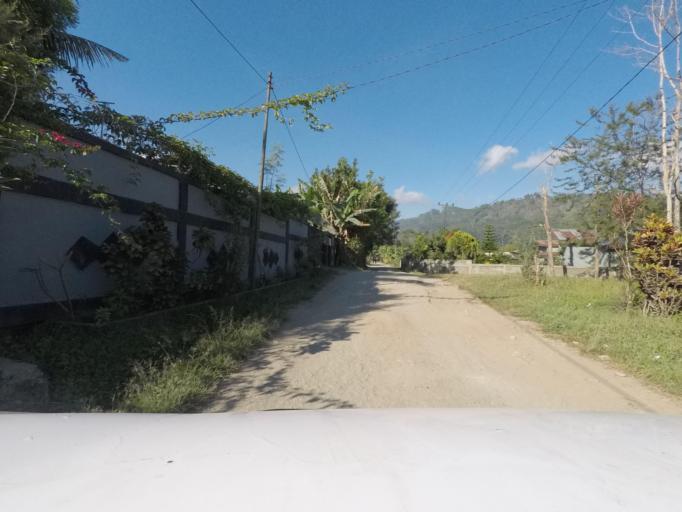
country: TL
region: Ermera
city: Gleno
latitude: -8.7262
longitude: 125.4307
